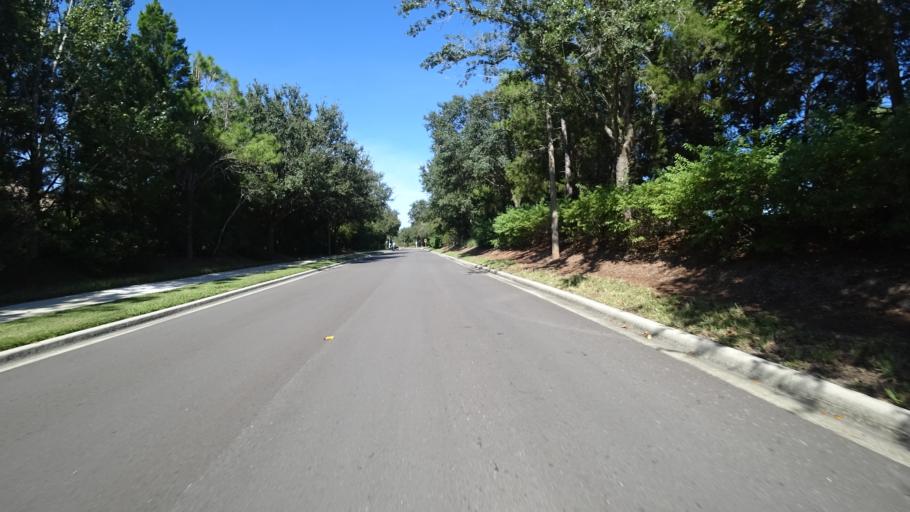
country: US
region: Florida
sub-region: Sarasota County
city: The Meadows
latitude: 27.4071
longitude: -82.4042
